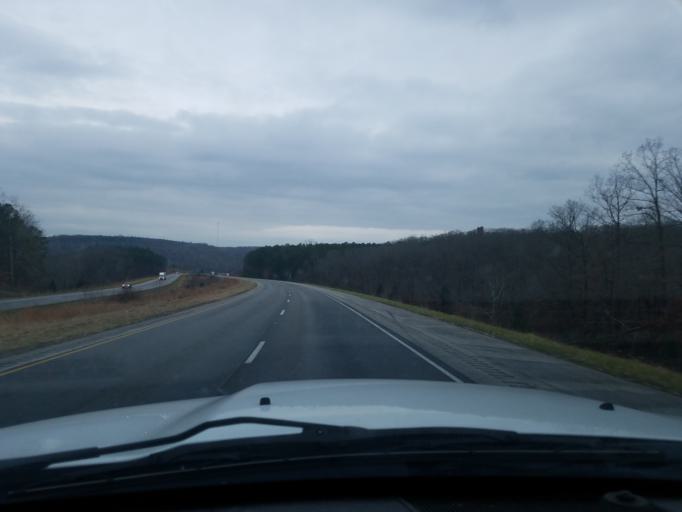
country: US
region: Indiana
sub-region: Crawford County
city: English
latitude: 38.2384
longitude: -86.5160
